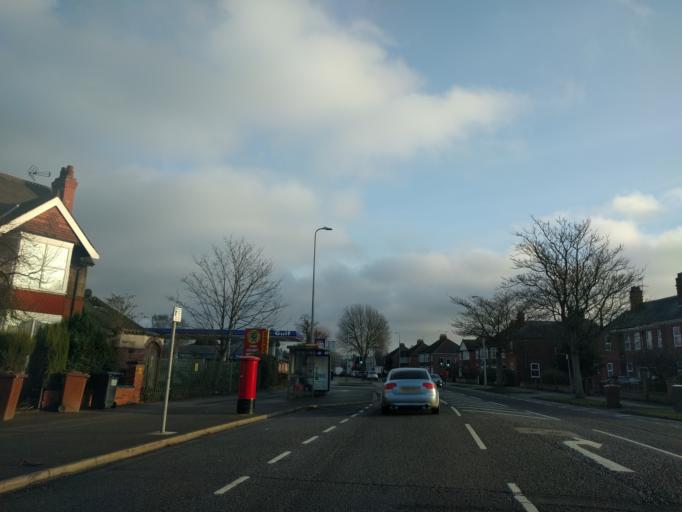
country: GB
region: England
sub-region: Lincolnshire
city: Lincoln
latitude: 53.2338
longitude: -0.5587
